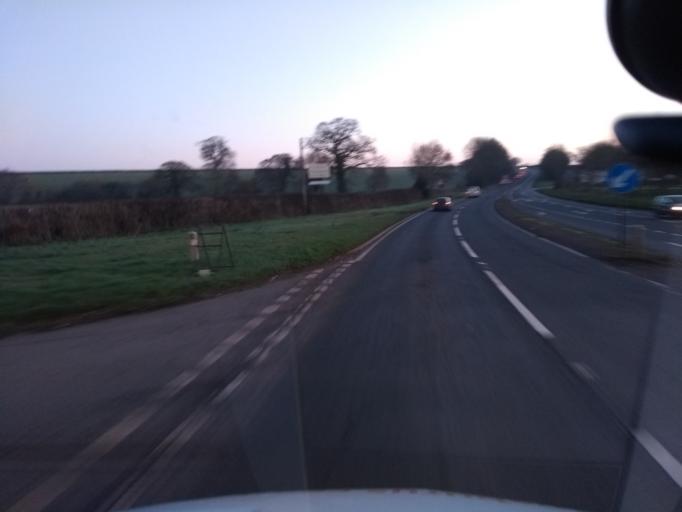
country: GB
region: England
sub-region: Somerset
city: North Petherton
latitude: 51.0632
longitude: -3.0308
